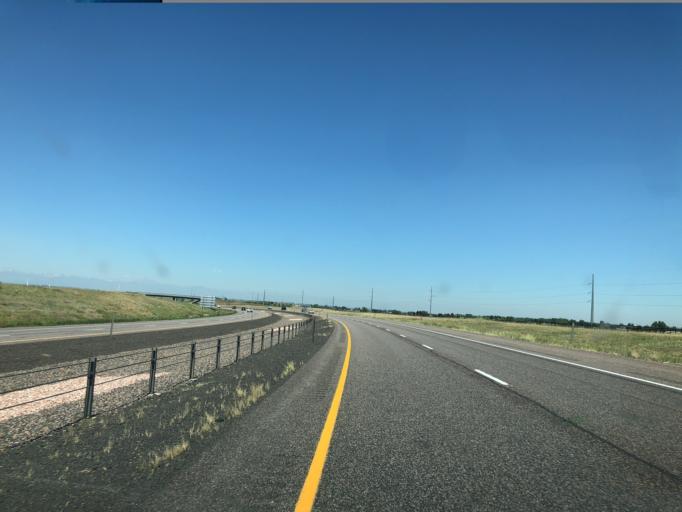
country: US
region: Colorado
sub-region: Adams County
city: Brighton
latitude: 39.9024
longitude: -104.7641
